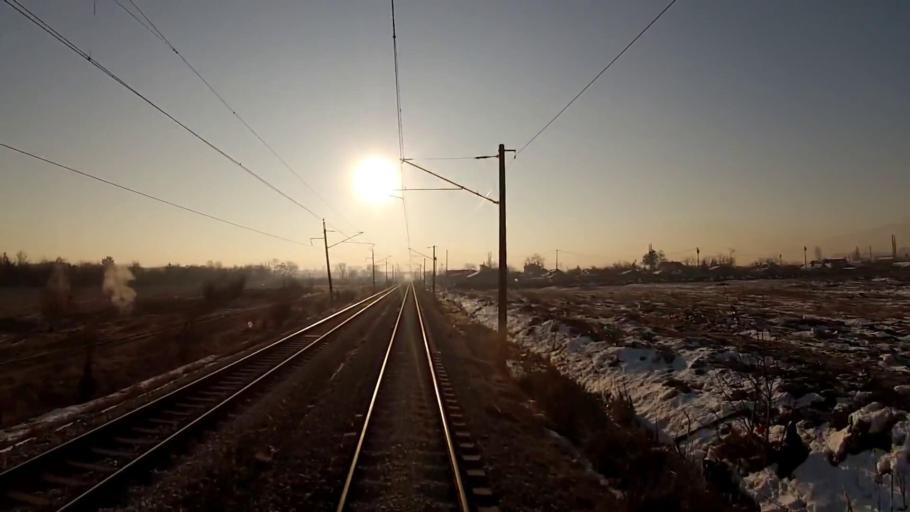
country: BG
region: Sofiya
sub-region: Obshtina Bozhurishte
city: Bozhurishte
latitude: 42.7395
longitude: 23.2628
